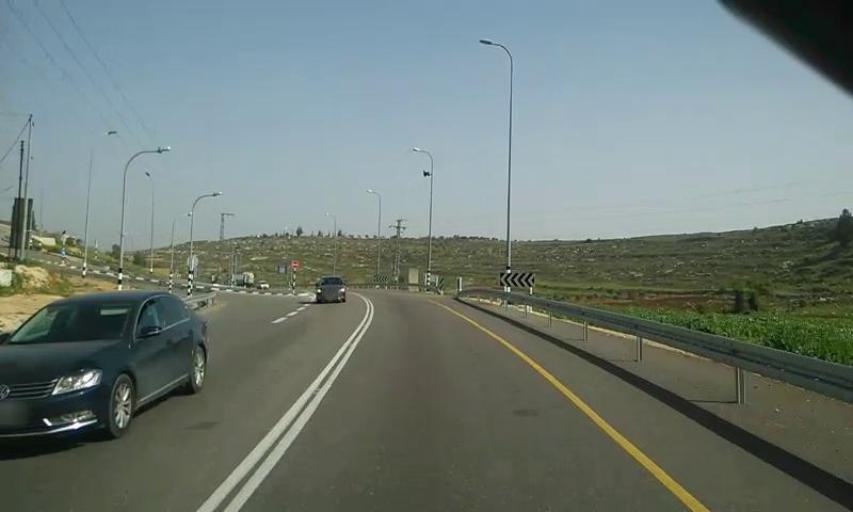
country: PS
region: West Bank
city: Sinjil
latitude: 32.0287
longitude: 35.2727
